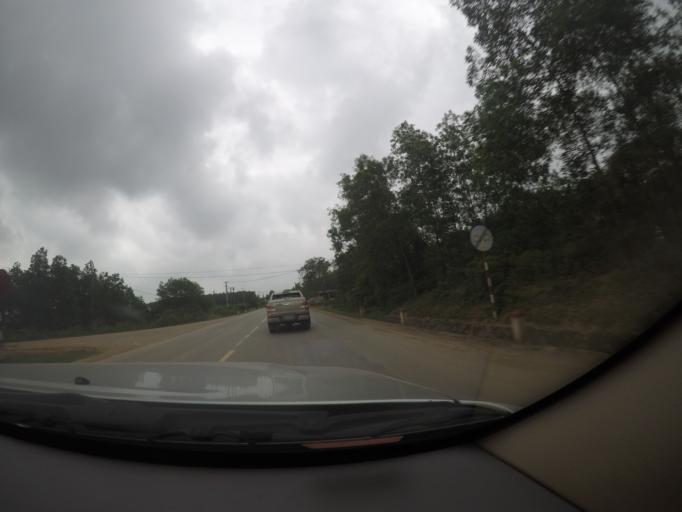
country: VN
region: Quang Tri
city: Cam Lo
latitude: 16.7970
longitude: 107.0467
